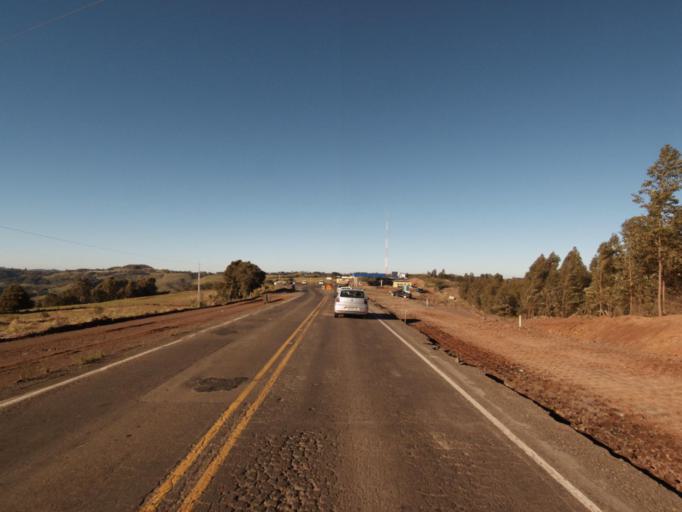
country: AR
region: Misiones
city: Bernardo de Irigoyen
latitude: -26.6357
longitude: -53.5189
